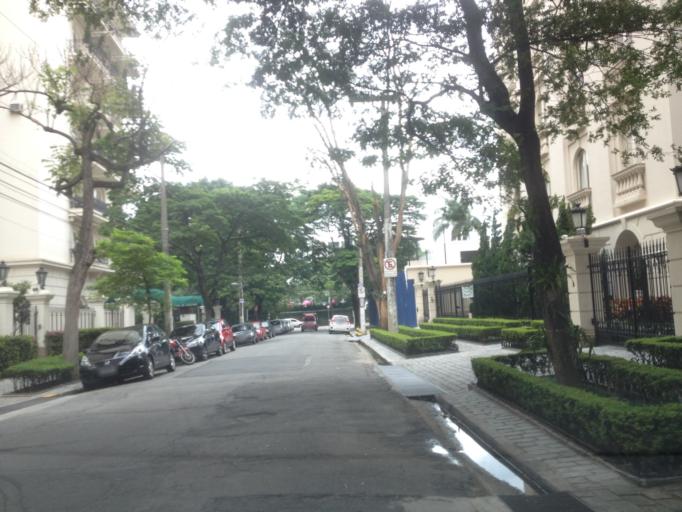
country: BR
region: Sao Paulo
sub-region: Sao Paulo
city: Sao Paulo
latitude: -23.5672
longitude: -46.6667
